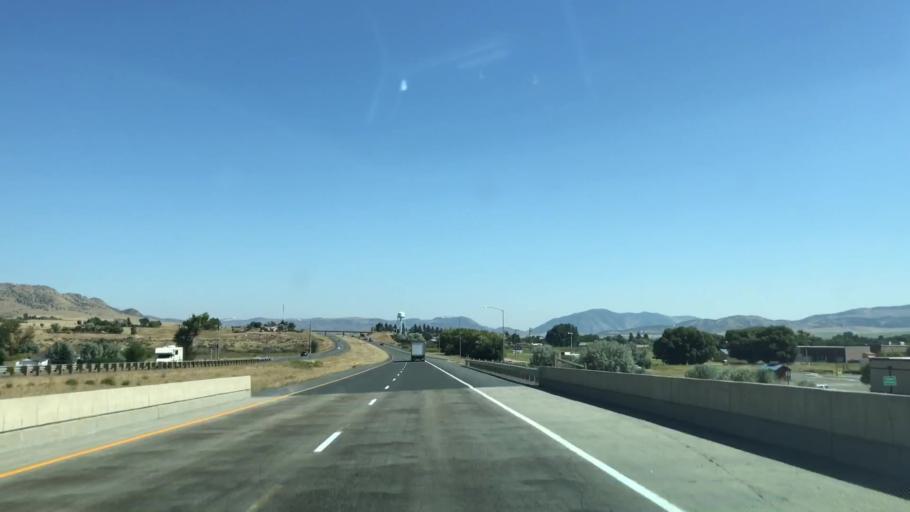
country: US
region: Montana
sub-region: Jefferson County
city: Whitehall
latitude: 45.8770
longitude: -112.1035
